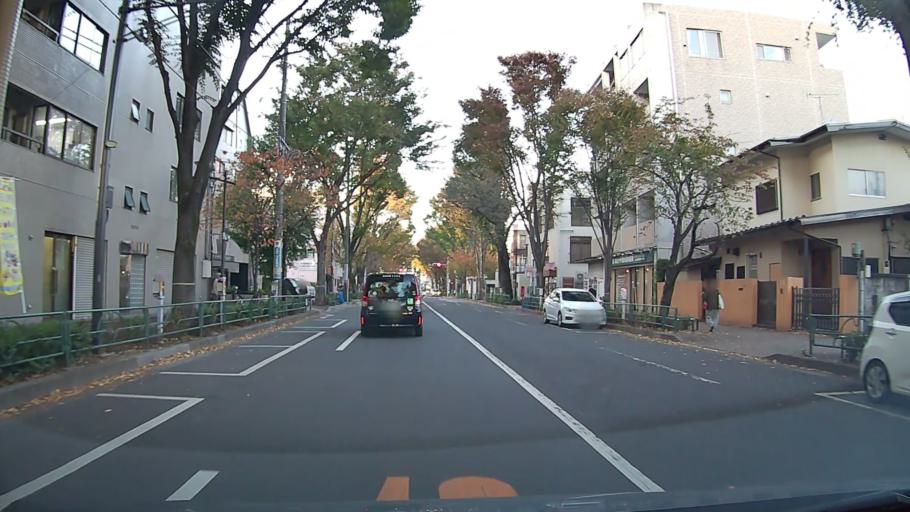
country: JP
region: Tokyo
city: Tokyo
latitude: 35.7117
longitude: 139.6351
